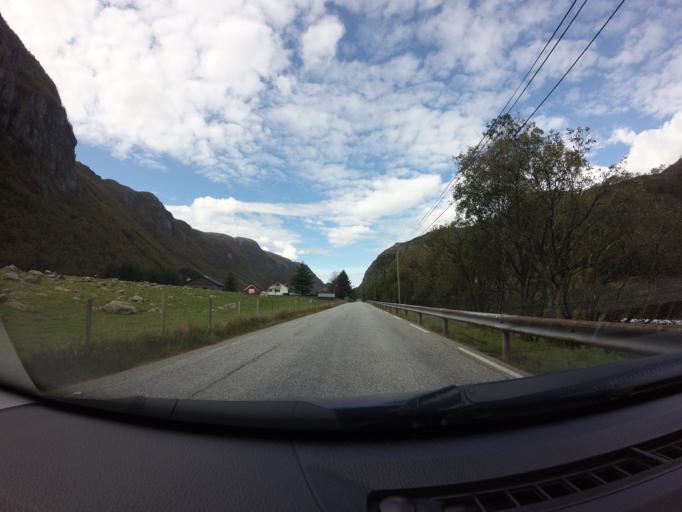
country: NO
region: Rogaland
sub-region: Forsand
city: Forsand
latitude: 58.8095
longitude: 6.2358
